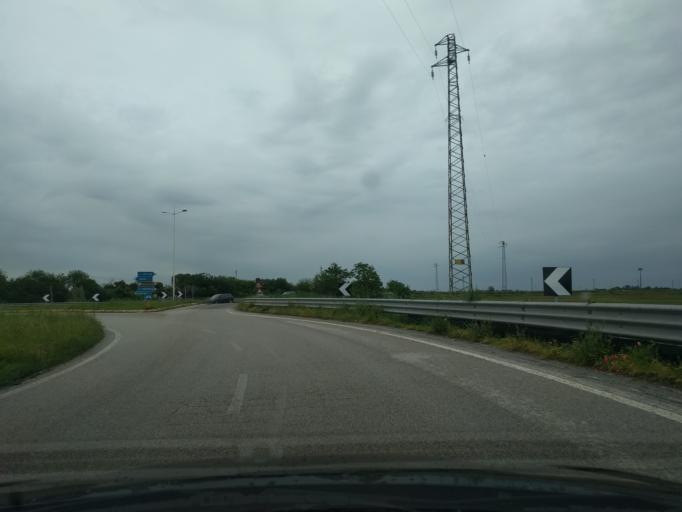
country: IT
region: Veneto
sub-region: Provincia di Rovigo
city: Loreo
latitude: 45.0517
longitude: 12.1544
